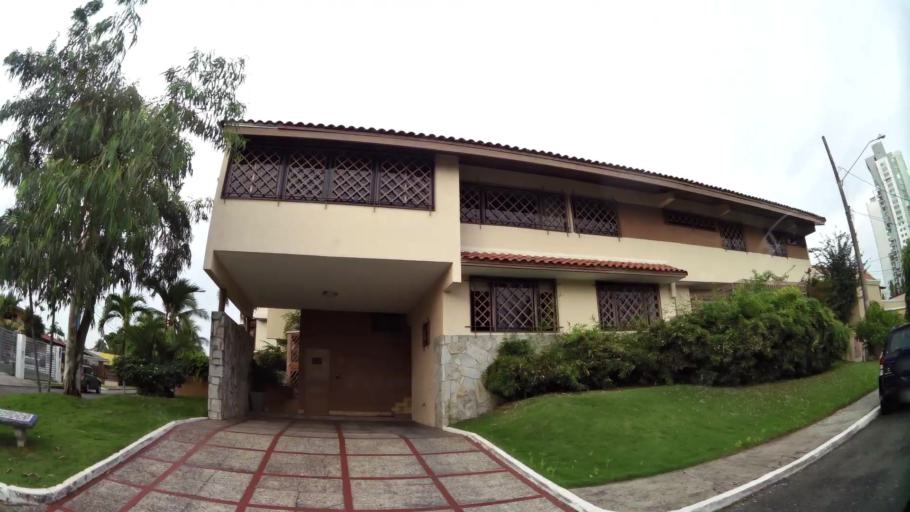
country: PA
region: Panama
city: Panama
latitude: 8.9976
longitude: -79.5002
